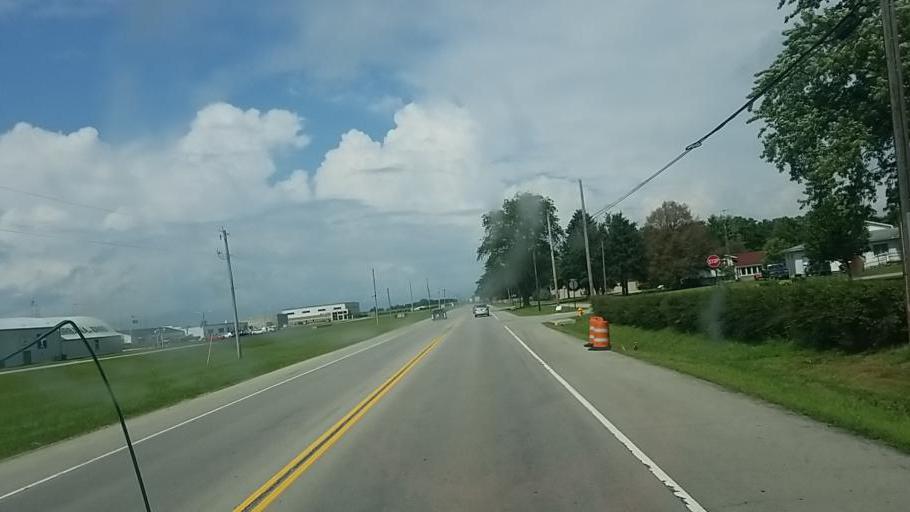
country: US
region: Ohio
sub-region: Champaign County
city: Urbana
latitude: 40.1308
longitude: -83.7483
